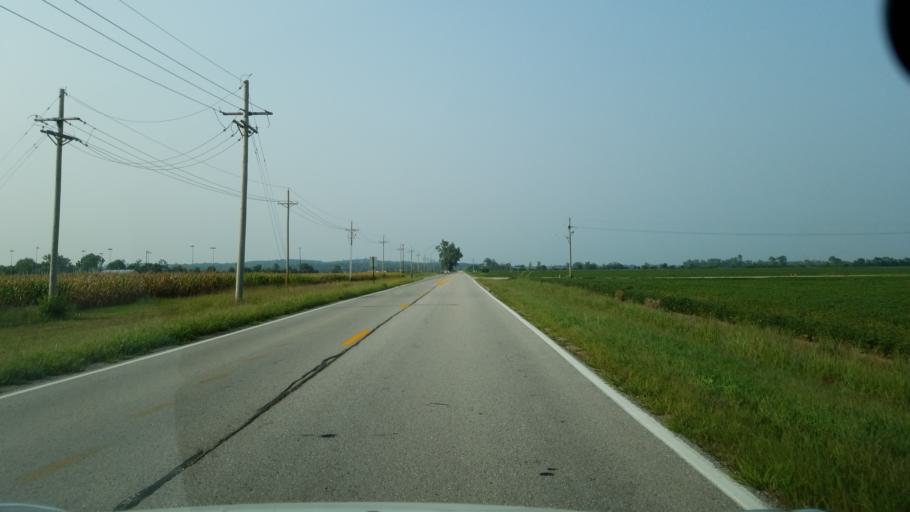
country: US
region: Nebraska
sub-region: Sarpy County
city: Bellevue
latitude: 41.0992
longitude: -95.8899
